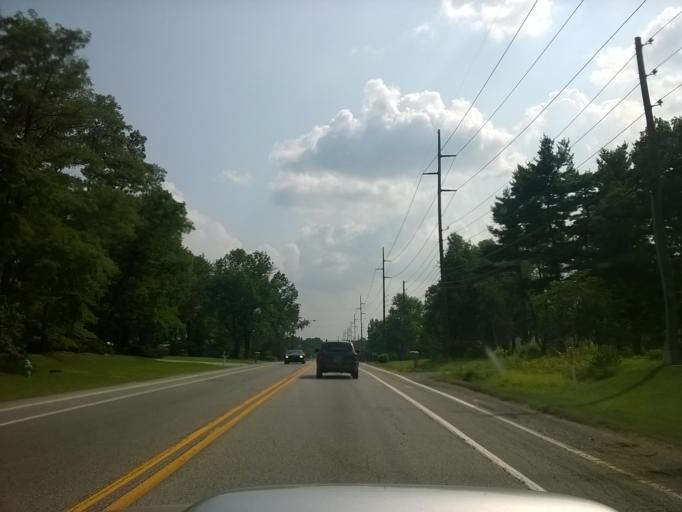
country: US
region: Indiana
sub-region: Marion County
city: Broad Ripple
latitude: 39.8728
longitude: -86.0950
